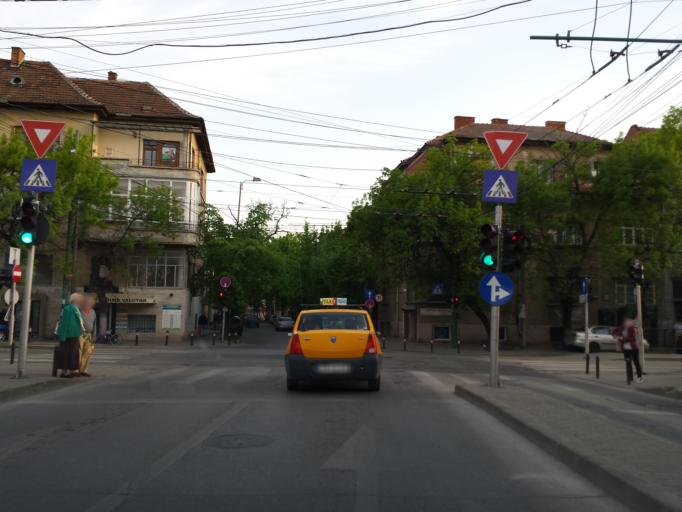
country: RO
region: Timis
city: Timisoara
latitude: 45.7565
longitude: 21.2233
